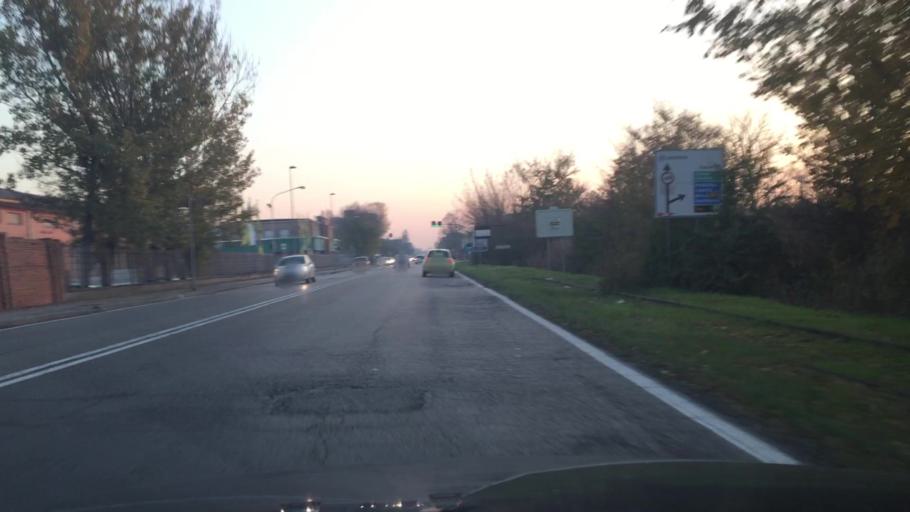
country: IT
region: Emilia-Romagna
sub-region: Provincia di Ferrara
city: Ferrara
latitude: 44.8561
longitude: 11.6007
